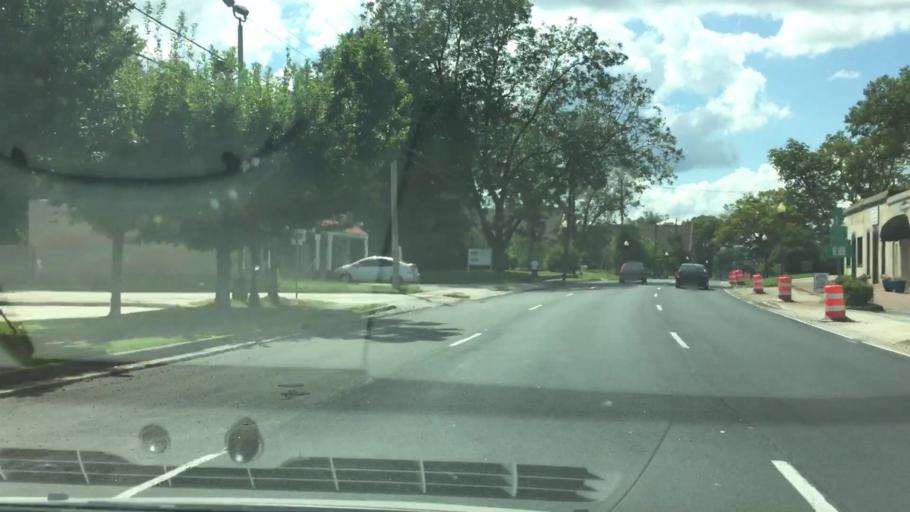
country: US
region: Georgia
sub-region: Fayette County
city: Fayetteville
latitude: 33.4488
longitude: -84.4503
